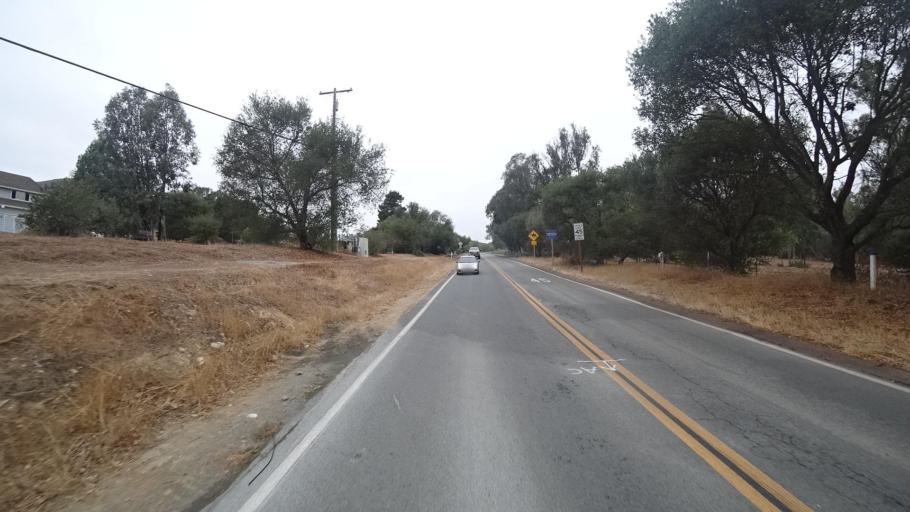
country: US
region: California
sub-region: San Diego County
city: Rancho Santa Fe
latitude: 33.0732
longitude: -117.1650
